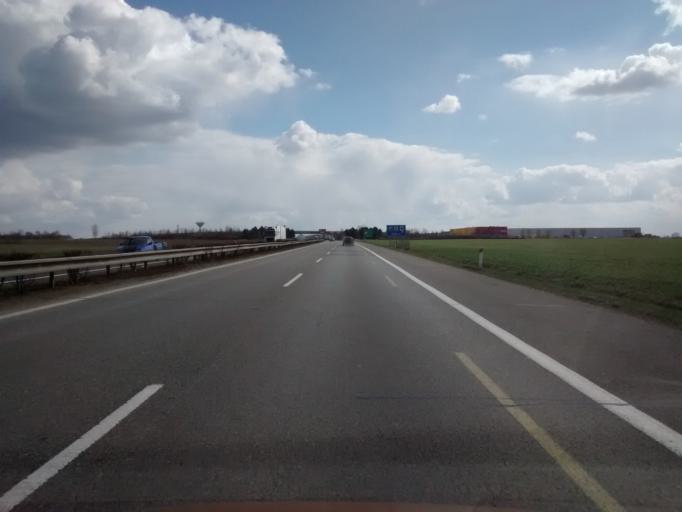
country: CZ
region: Central Bohemia
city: Zdiby
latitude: 50.1895
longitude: 14.4437
